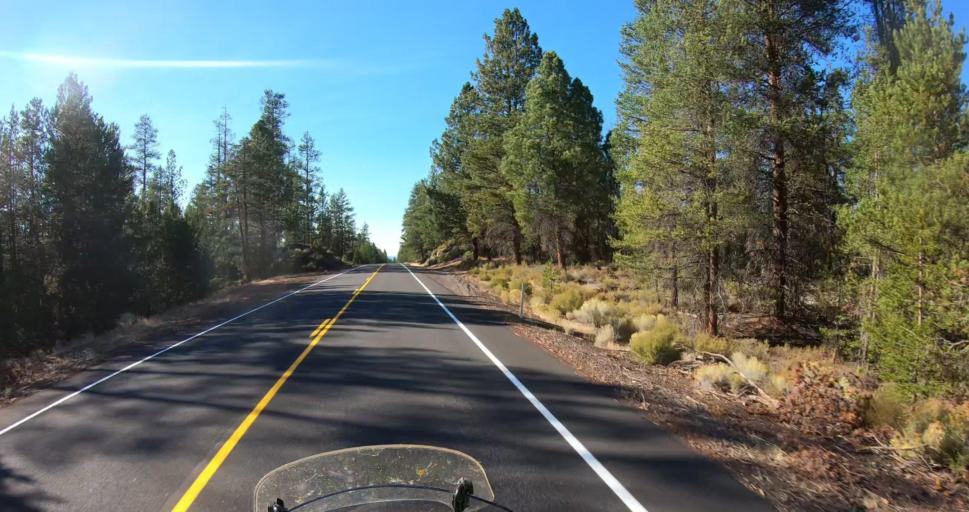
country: US
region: Oregon
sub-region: Deschutes County
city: La Pine
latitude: 43.4864
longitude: -121.4293
